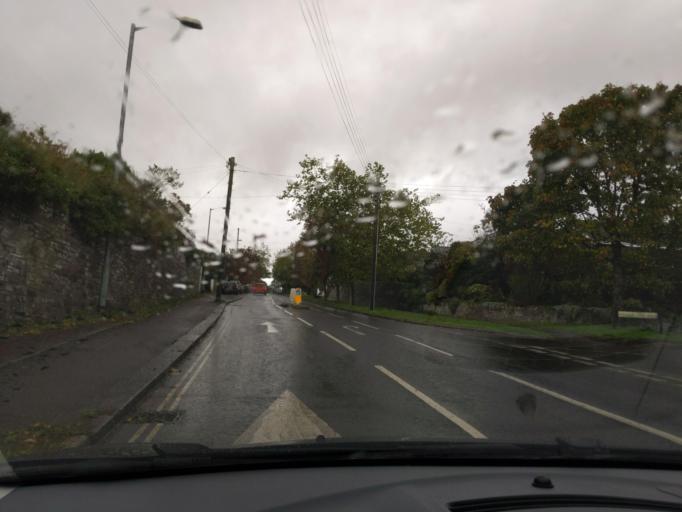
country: GB
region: England
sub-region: Cornwall
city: Wadebridge
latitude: 50.5170
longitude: -4.8418
